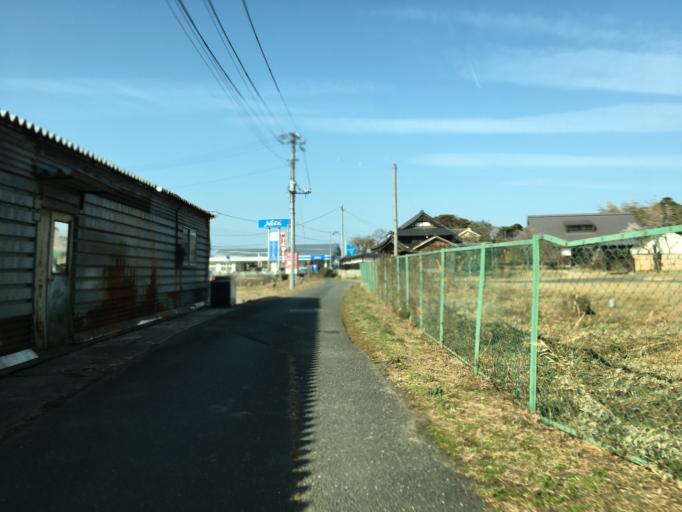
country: JP
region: Ibaraki
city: Takahagi
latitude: 36.7497
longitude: 140.7304
